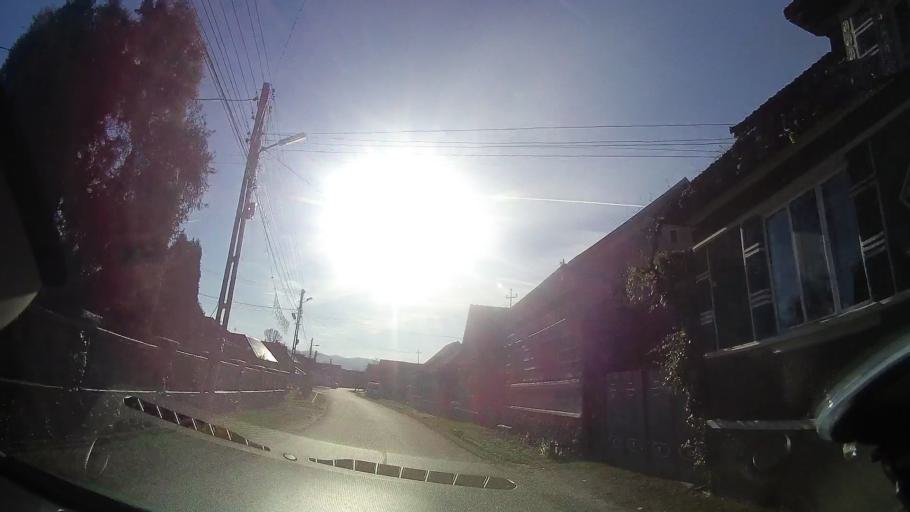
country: RO
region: Bihor
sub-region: Comuna Auseu
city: Grosi
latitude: 47.0265
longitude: 22.4736
